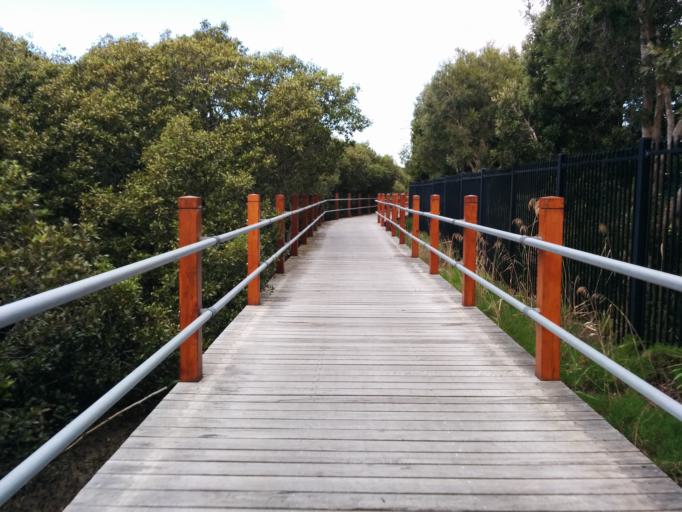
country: AU
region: New South Wales
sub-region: Sutherland Shire
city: Caringbah
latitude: -34.0355
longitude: 151.1360
